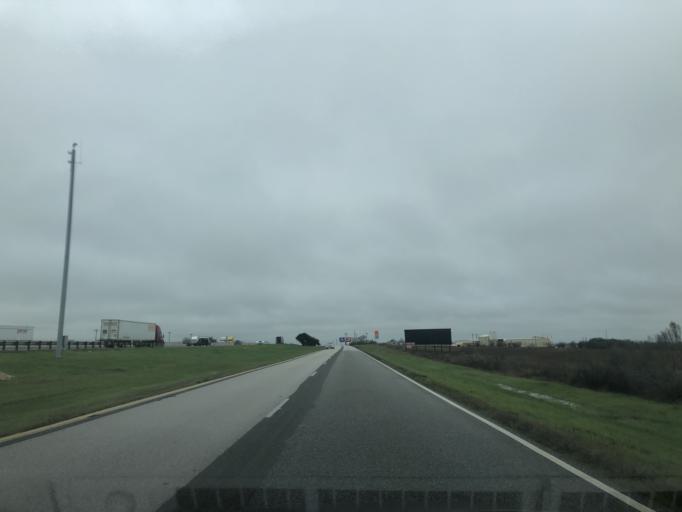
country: US
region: Texas
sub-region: Williamson County
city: Serenada
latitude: 30.7572
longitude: -97.6333
